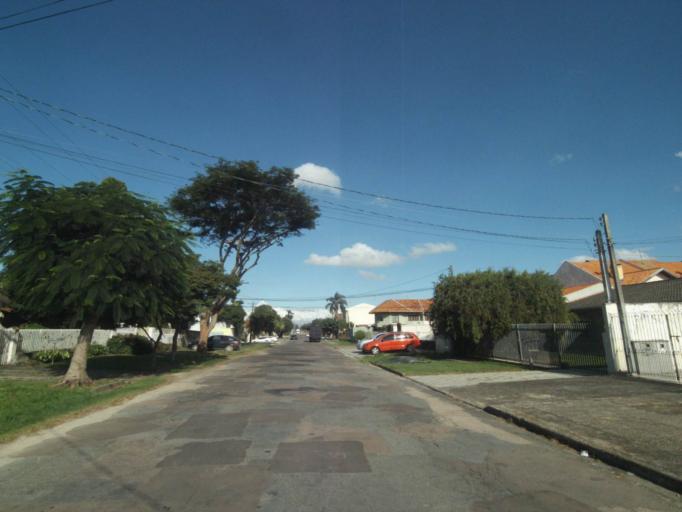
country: BR
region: Parana
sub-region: Pinhais
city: Pinhais
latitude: -25.4354
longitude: -49.2128
